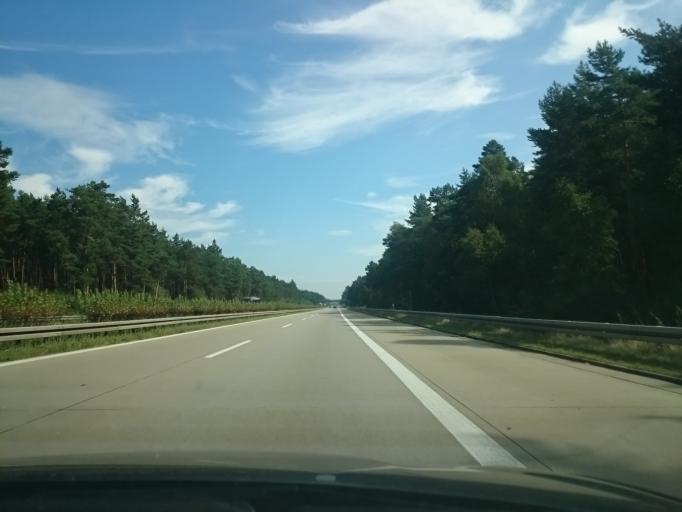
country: DE
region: Brandenburg
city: Ortrand
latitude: 51.3927
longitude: 13.7587
